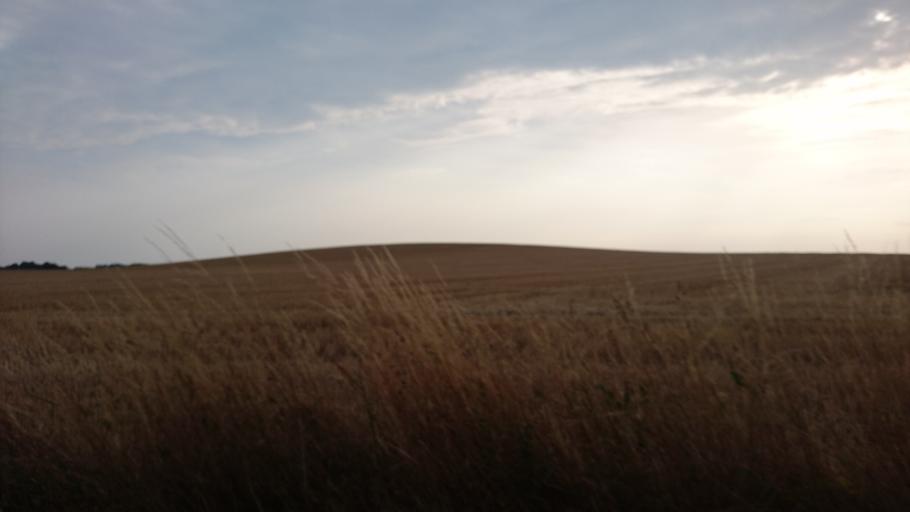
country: DK
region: Zealand
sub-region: Vordingborg Kommune
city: Stege
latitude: 54.9792
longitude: 12.4400
